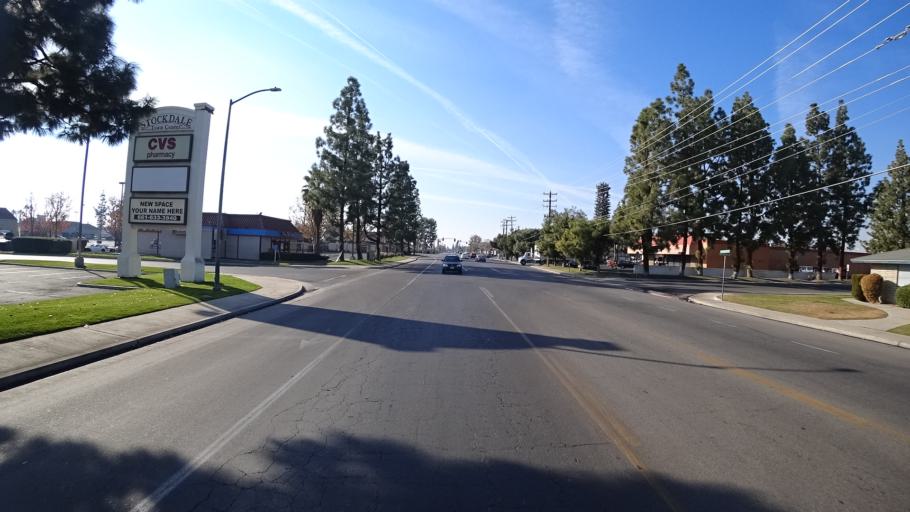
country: US
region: California
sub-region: Kern County
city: Bakersfield
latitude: 35.3250
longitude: -119.0549
